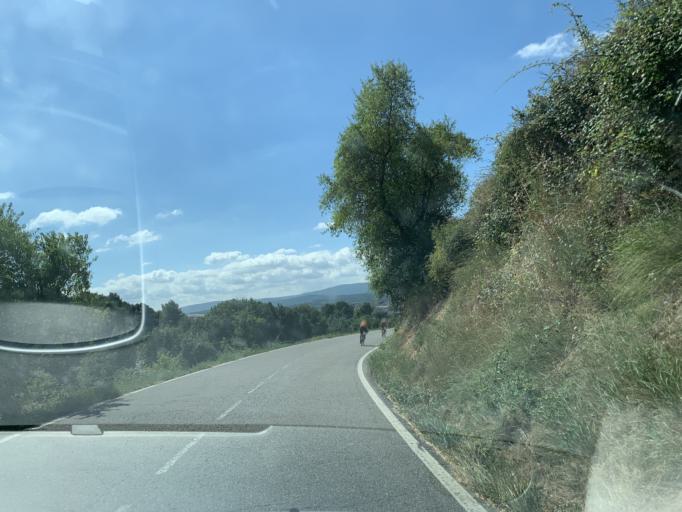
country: ES
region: Catalonia
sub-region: Provincia de Tarragona
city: Santa Coloma de Queralt
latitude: 41.5414
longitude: 1.3736
